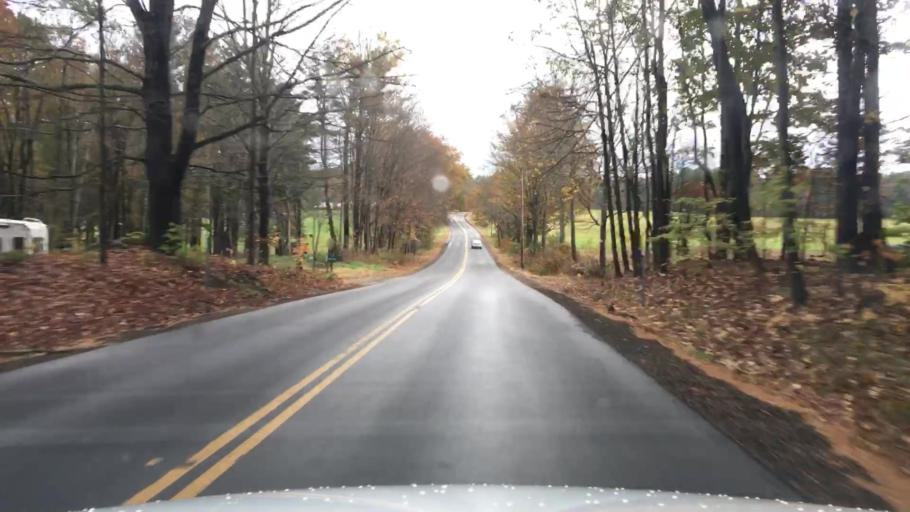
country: US
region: New Hampshire
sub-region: Strafford County
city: Lee
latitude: 43.1192
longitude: -71.0096
